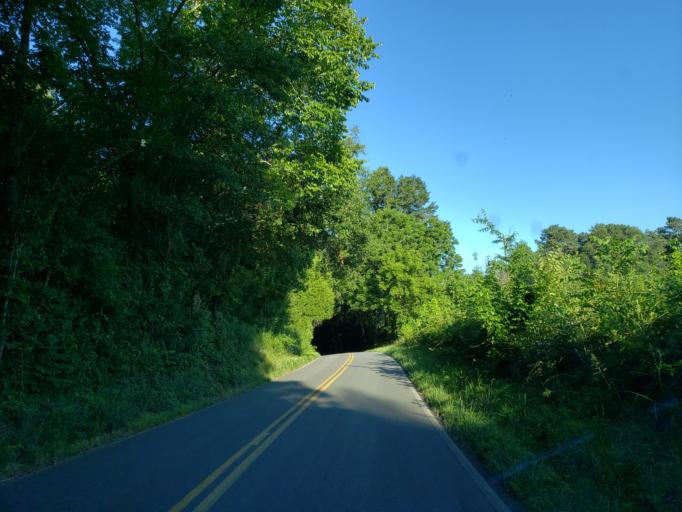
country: US
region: Georgia
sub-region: Polk County
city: Aragon
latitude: 34.0864
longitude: -85.0306
